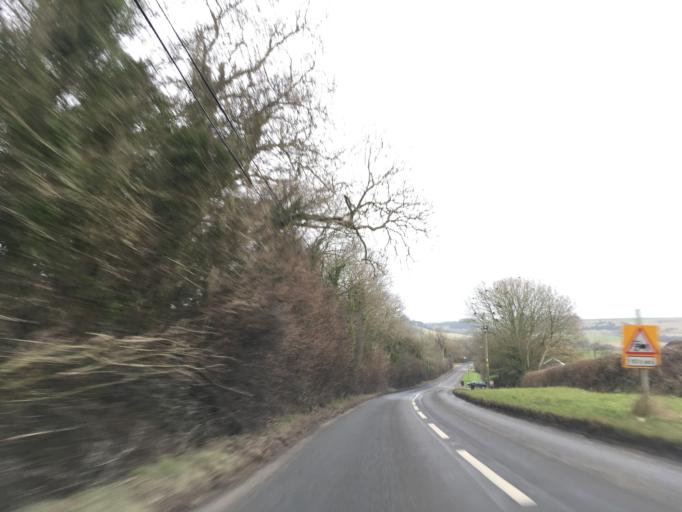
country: GB
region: England
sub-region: South Gloucestershire
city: Hinton
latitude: 51.5068
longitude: -2.3878
